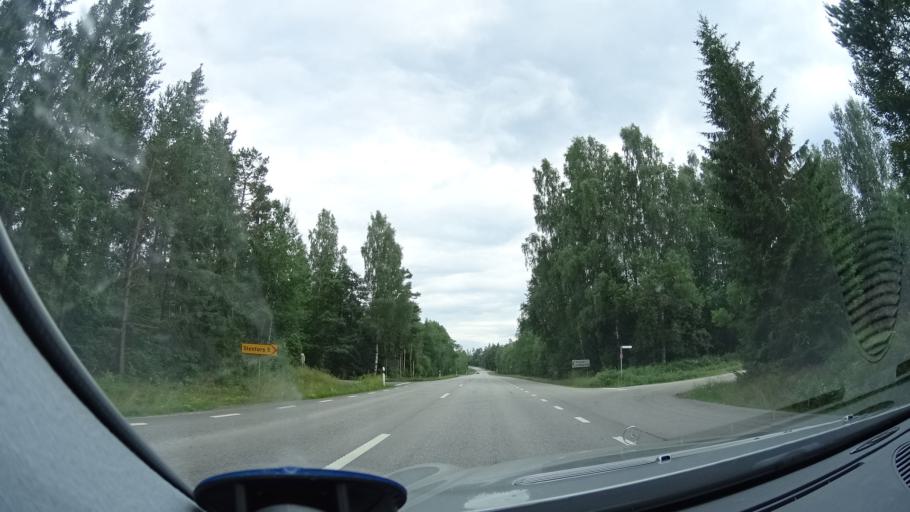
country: SE
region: Kronoberg
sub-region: Tingsryds Kommun
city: Tingsryd
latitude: 56.5003
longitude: 14.9956
